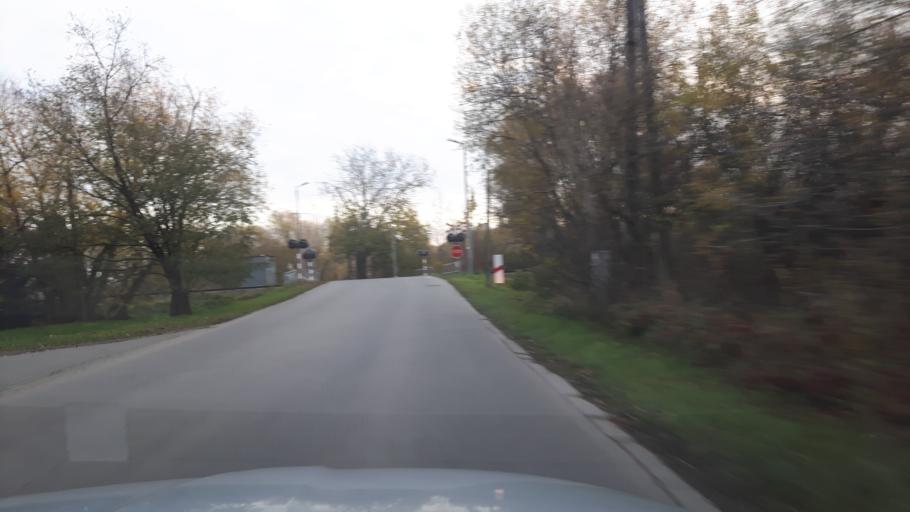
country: PL
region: Masovian Voivodeship
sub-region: Warszawa
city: Wilanow
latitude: 52.1821
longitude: 21.0986
